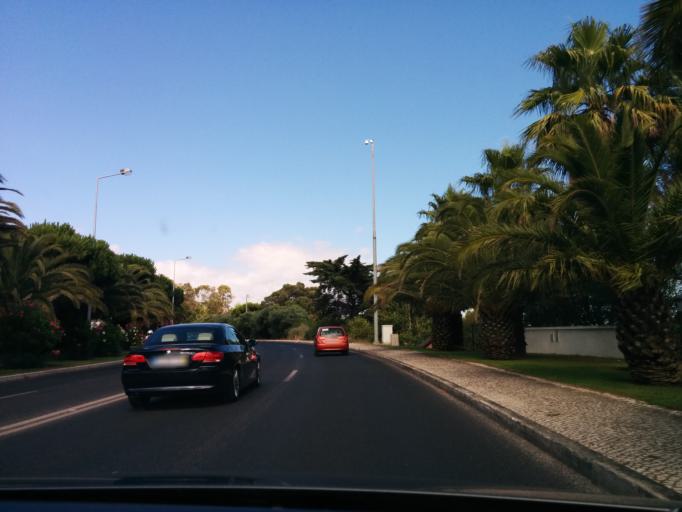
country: PT
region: Lisbon
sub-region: Oeiras
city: Carcavelos
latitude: 38.6776
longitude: -9.3197
